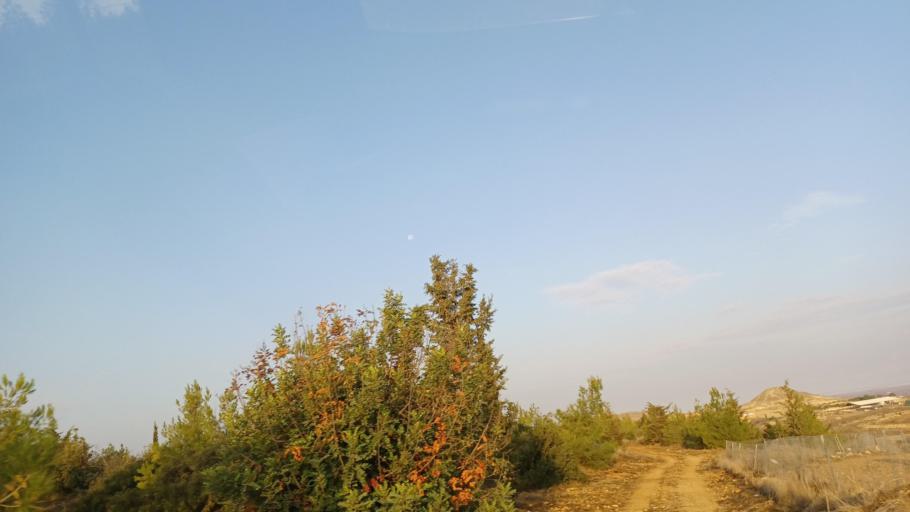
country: CY
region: Larnaka
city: Athienou
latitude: 35.0238
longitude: 33.5467
